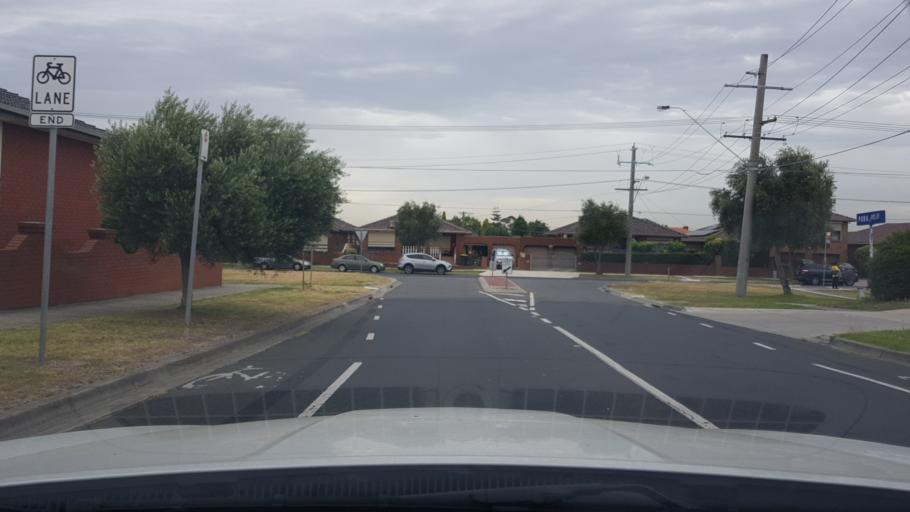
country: AU
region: Victoria
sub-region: Whittlesea
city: Lalor
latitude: -37.6709
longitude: 144.9946
